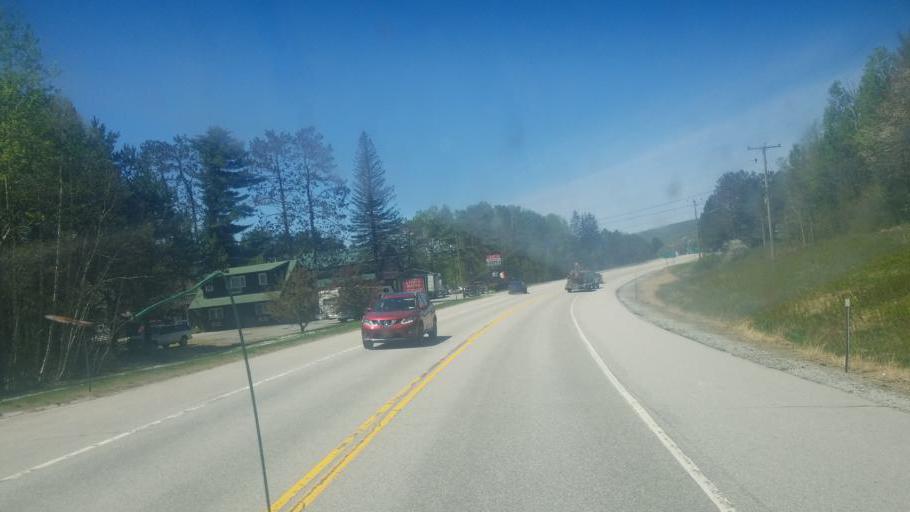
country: US
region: New Hampshire
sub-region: Grafton County
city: Deerfield
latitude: 44.2693
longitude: -71.5349
